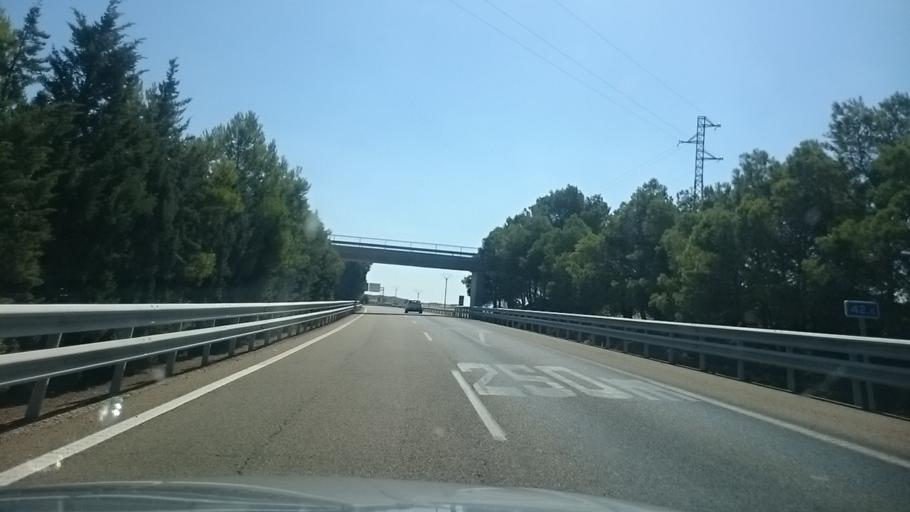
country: ES
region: Aragon
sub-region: Provincia de Zaragoza
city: Pina de Ebro
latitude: 41.5241
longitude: -0.4574
